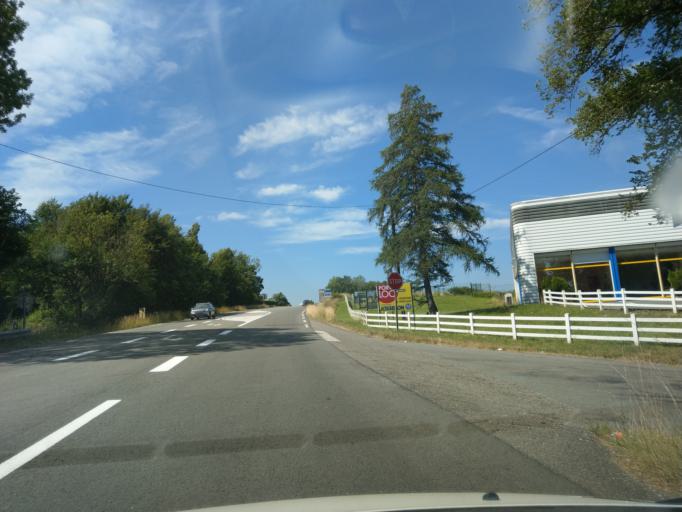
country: FR
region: Franche-Comte
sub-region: Territoire de Belfort
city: Offemont
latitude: 47.6642
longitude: 6.9111
